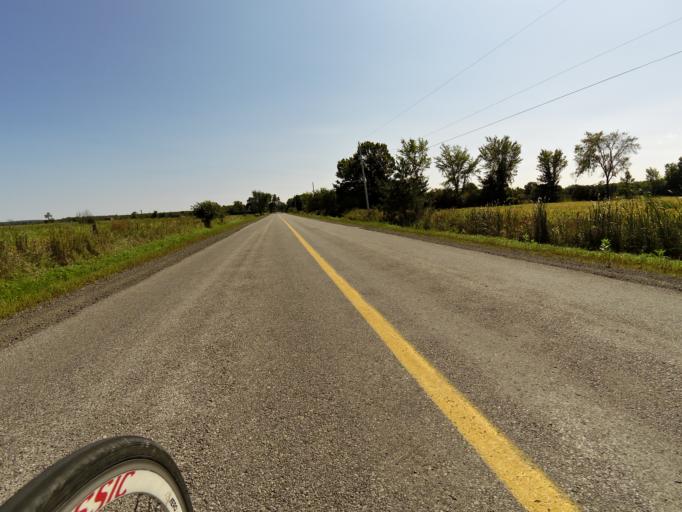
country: CA
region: Ontario
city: Bells Corners
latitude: 45.4423
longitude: -76.0733
